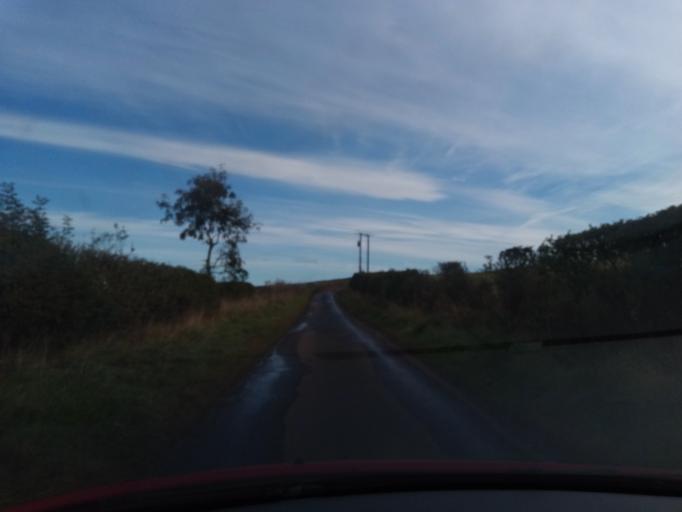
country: GB
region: Scotland
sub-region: The Scottish Borders
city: Kelso
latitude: 55.5081
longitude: -2.4185
